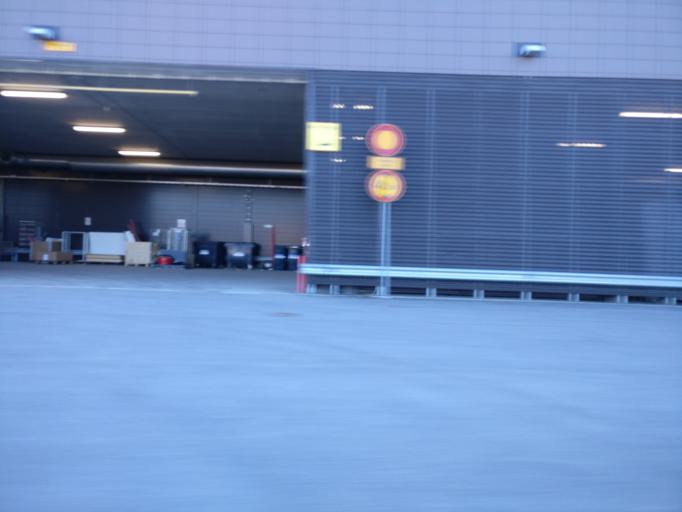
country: FI
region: Uusimaa
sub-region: Helsinki
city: Vantaa
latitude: 60.2800
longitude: 25.0828
